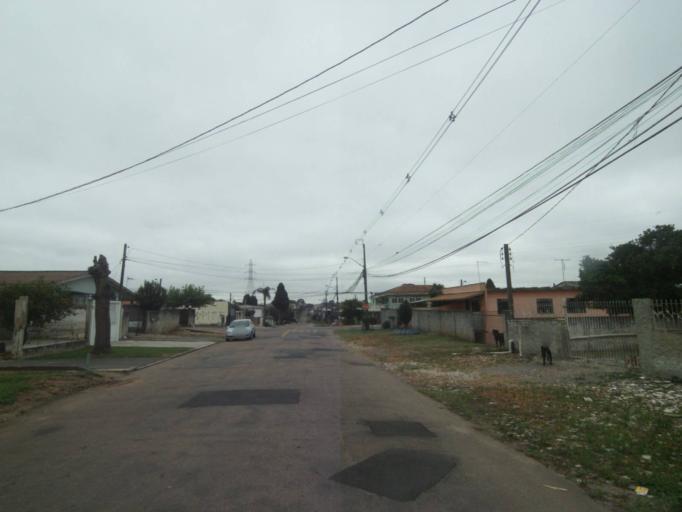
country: BR
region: Parana
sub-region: Sao Jose Dos Pinhais
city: Sao Jose dos Pinhais
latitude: -25.5411
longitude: -49.2831
